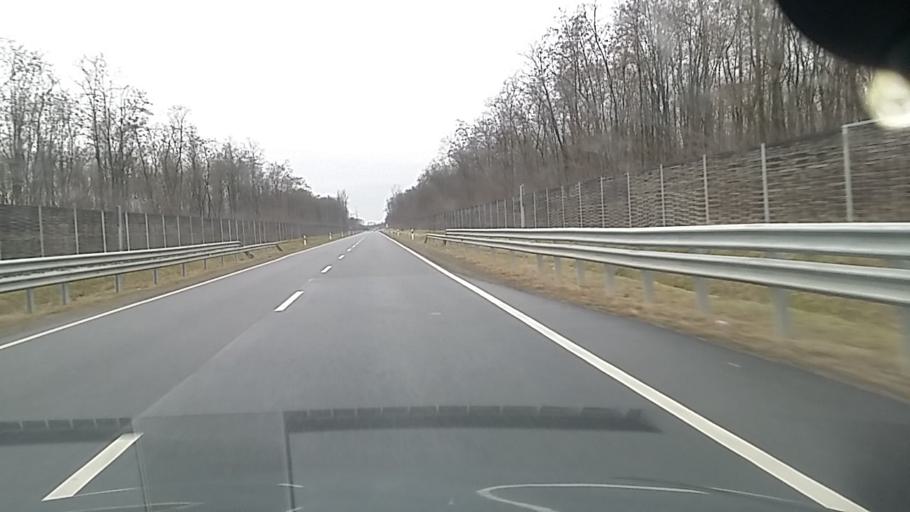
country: HU
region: Hajdu-Bihar
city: Debrecen
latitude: 47.5857
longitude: 21.6068
